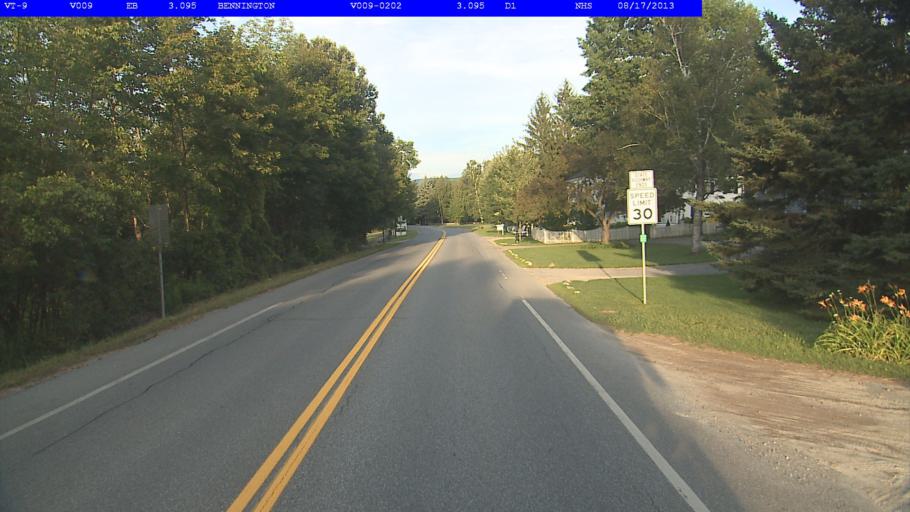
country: US
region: Vermont
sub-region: Bennington County
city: Bennington
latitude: 42.8821
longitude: -73.2186
